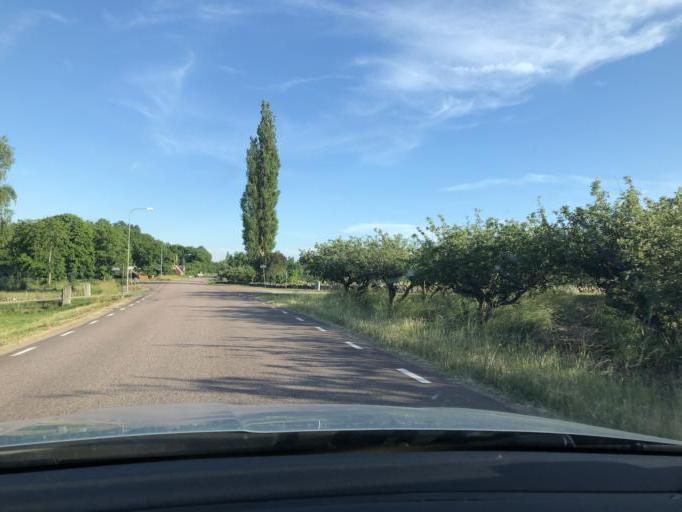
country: SE
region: Blekinge
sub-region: Solvesborgs Kommun
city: Soelvesborg
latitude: 56.1551
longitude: 14.6012
